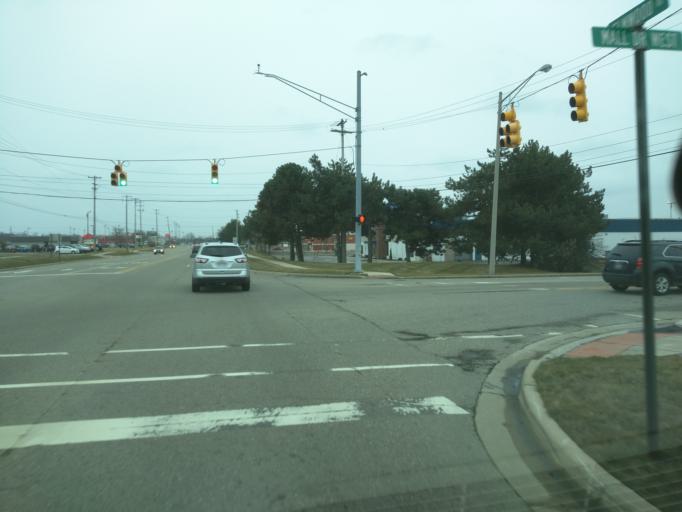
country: US
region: Michigan
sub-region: Eaton County
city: Waverly
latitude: 42.7455
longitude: -84.6226
